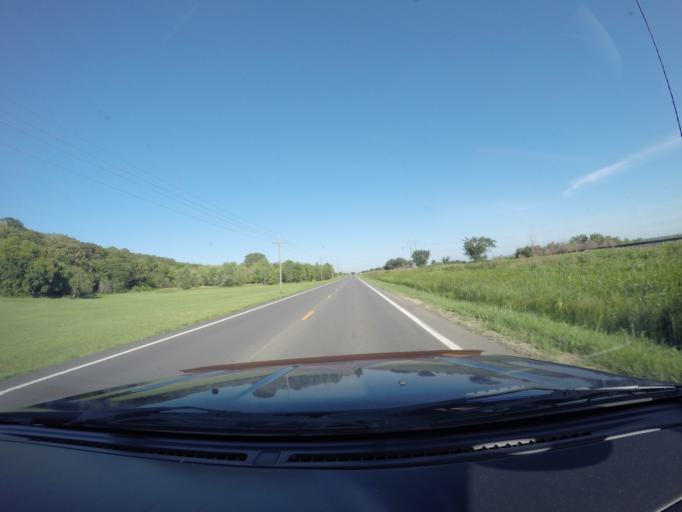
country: US
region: Kansas
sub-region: Douglas County
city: Lawrence
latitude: 39.0379
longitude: -95.2590
